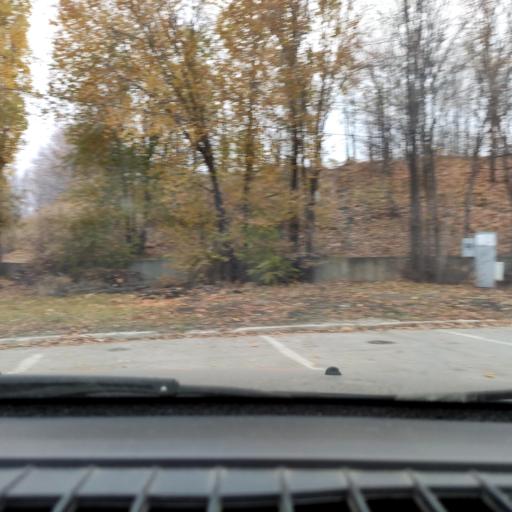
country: RU
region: Samara
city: Tol'yatti
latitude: 53.5014
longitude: 49.2532
